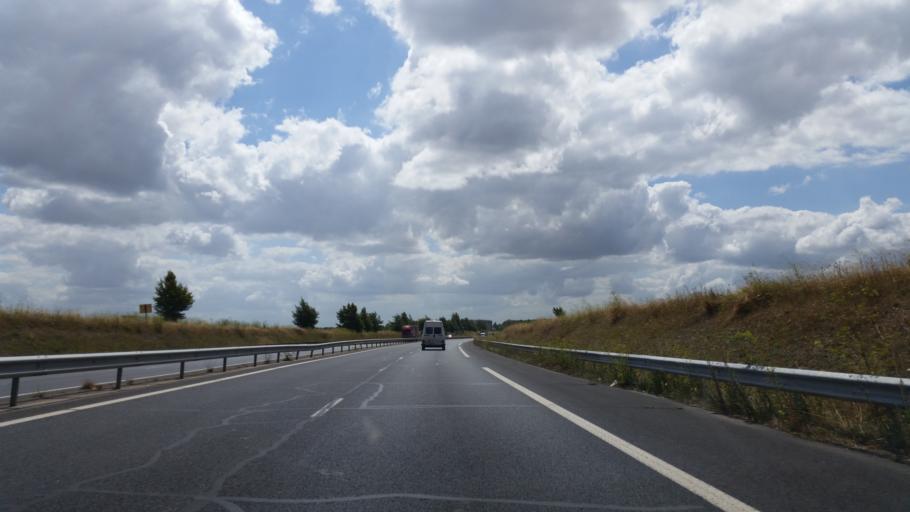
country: FR
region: Lower Normandy
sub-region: Departement du Calvados
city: Falaise
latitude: 48.9197
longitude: -0.2058
